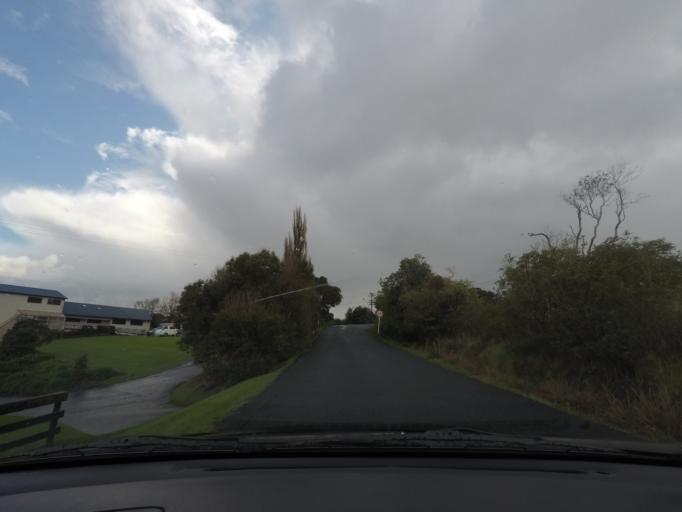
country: NZ
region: Auckland
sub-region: Auckland
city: Warkworth
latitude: -36.4284
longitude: 174.7318
